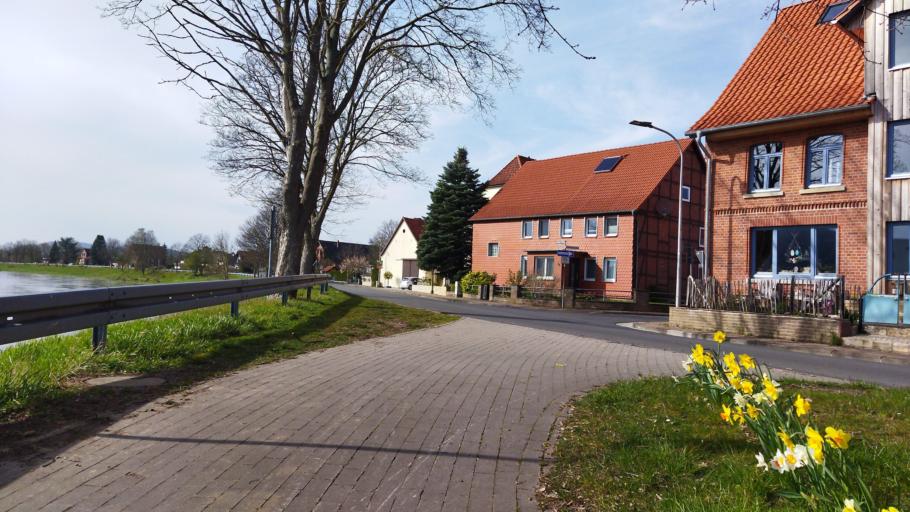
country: DE
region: Lower Saxony
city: Hessisch Oldendorf
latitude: 52.1750
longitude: 9.1875
